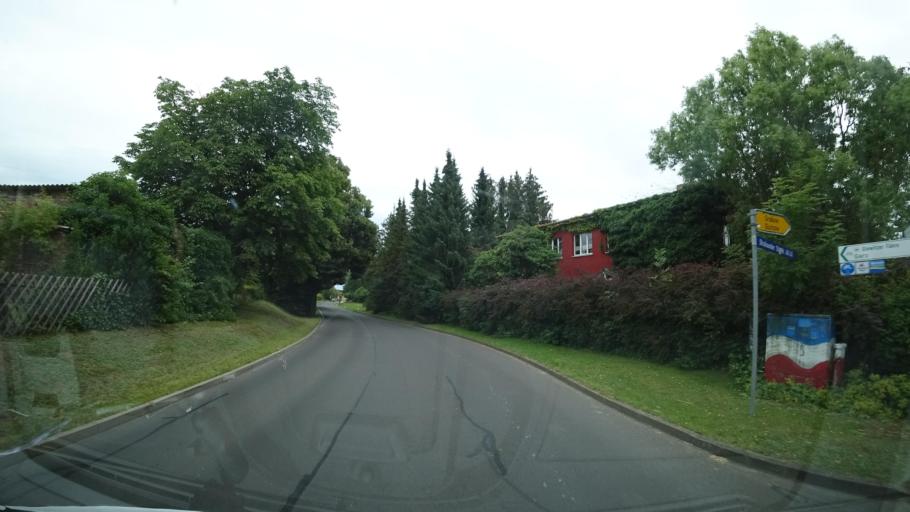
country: DE
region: Mecklenburg-Vorpommern
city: Poseritz
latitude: 54.2967
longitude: 13.2767
